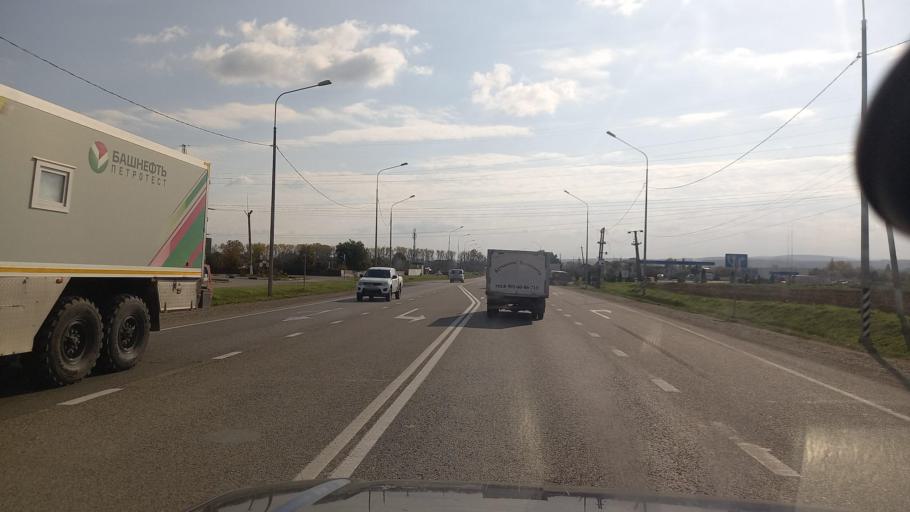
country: RU
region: Krasnodarskiy
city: Novoukrainskiy
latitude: 44.9054
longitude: 38.0289
